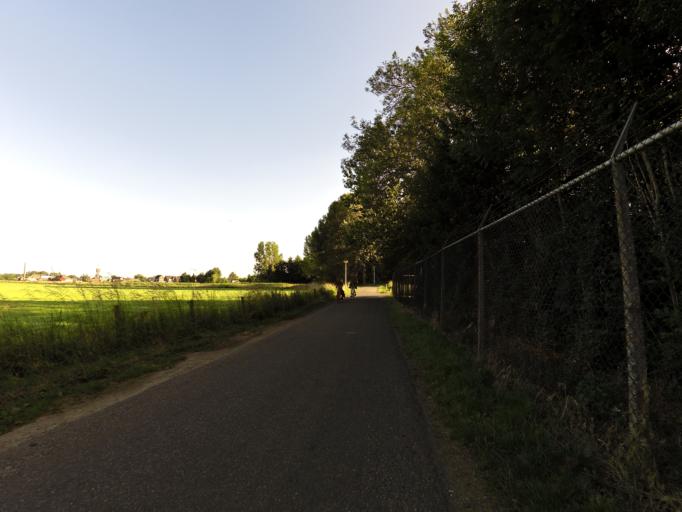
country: NL
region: Gelderland
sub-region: Oude IJsselstreek
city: Gendringen
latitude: 51.9035
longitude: 6.3789
